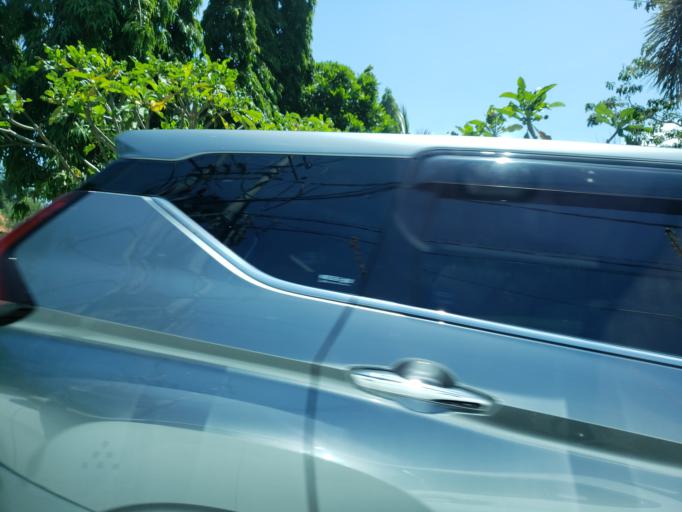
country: ID
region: Bali
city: Kangin
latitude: -8.8346
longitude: 115.1262
